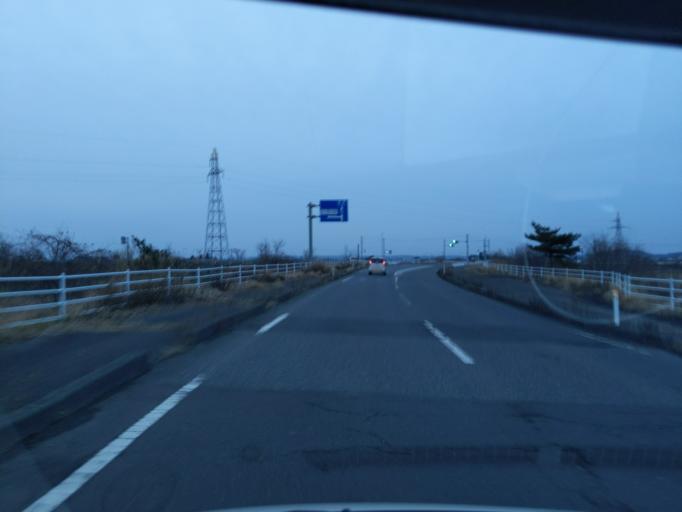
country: JP
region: Miyagi
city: Wakuya
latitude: 38.7260
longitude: 141.1482
